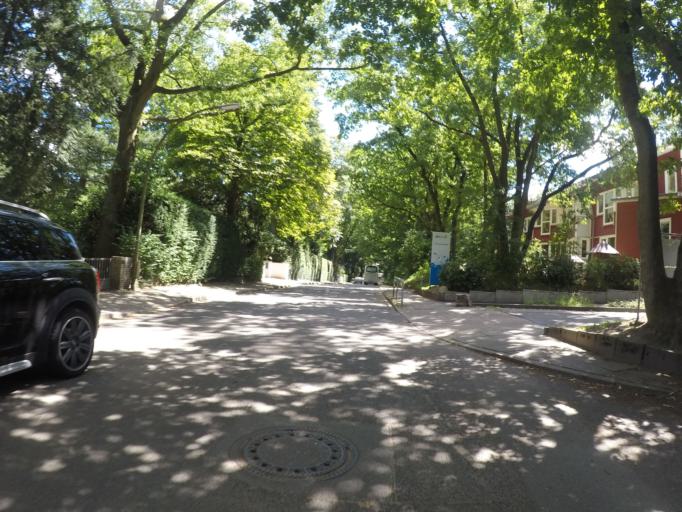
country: DE
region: Schleswig-Holstein
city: Halstenbek
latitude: 53.5728
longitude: 9.8015
